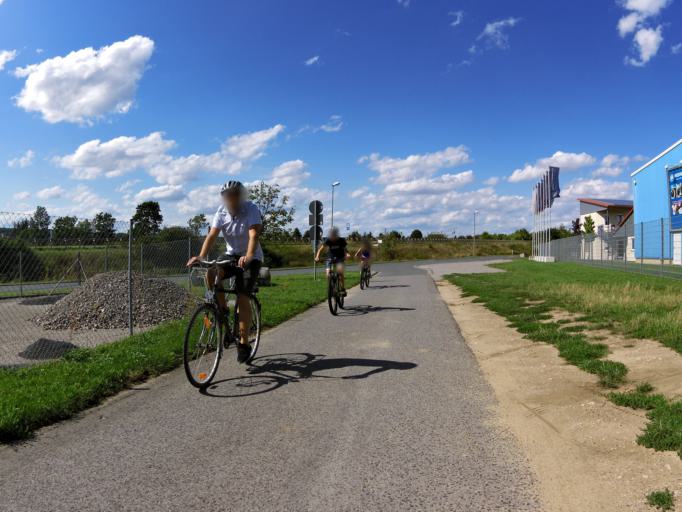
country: DE
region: Bavaria
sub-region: Regierungsbezirk Unterfranken
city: Marktsteft
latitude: 49.6890
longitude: 10.1446
